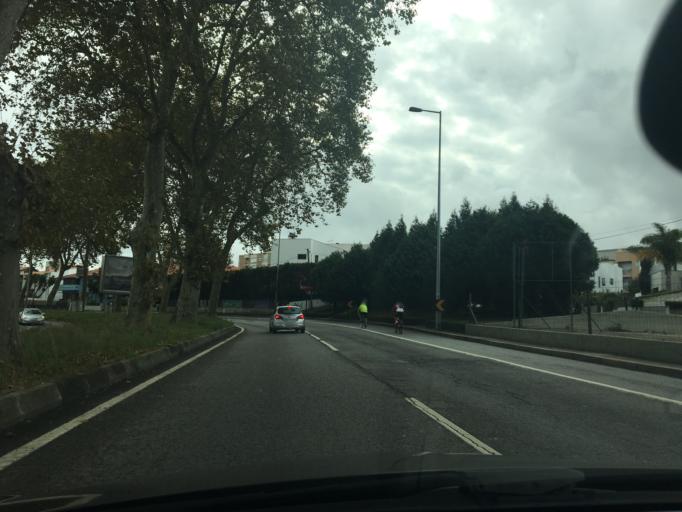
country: PT
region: Porto
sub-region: Matosinhos
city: Senhora da Hora
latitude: 41.1794
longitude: -8.6331
